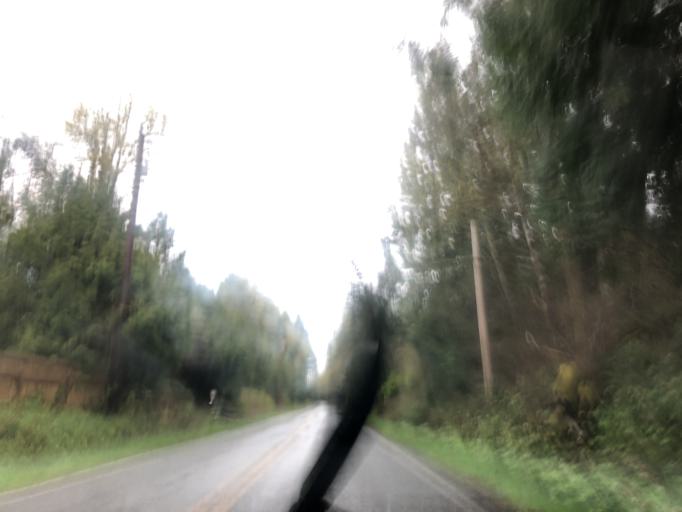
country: US
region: Washington
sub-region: Thurston County
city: Olympia
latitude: 47.1243
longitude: -122.8704
